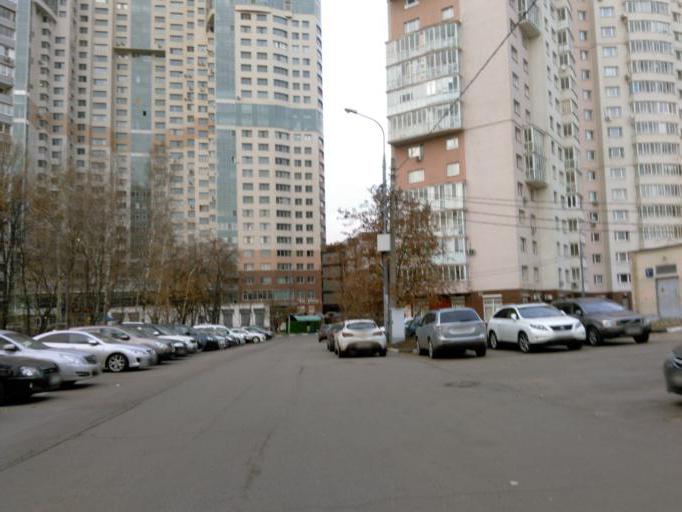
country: RU
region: Moscow
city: Troparevo
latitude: 55.6599
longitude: 37.5098
